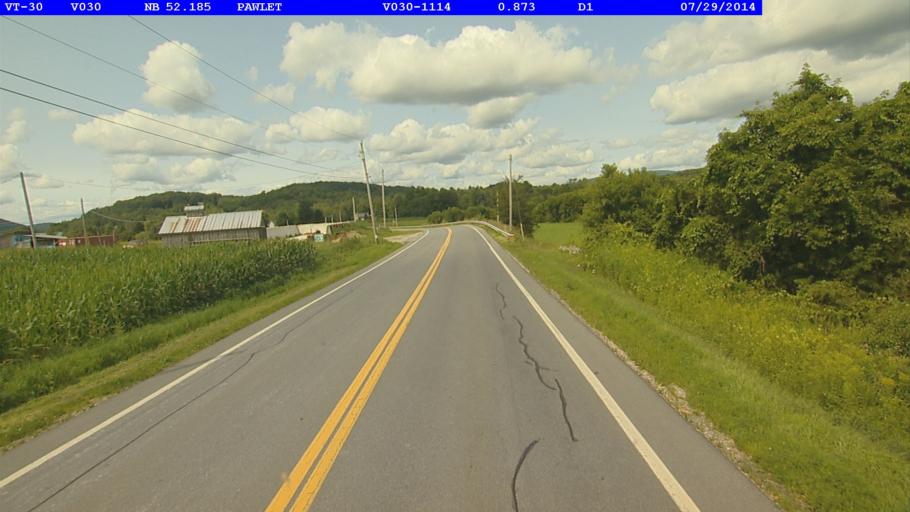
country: US
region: New York
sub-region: Washington County
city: Granville
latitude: 43.3234
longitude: -73.1719
